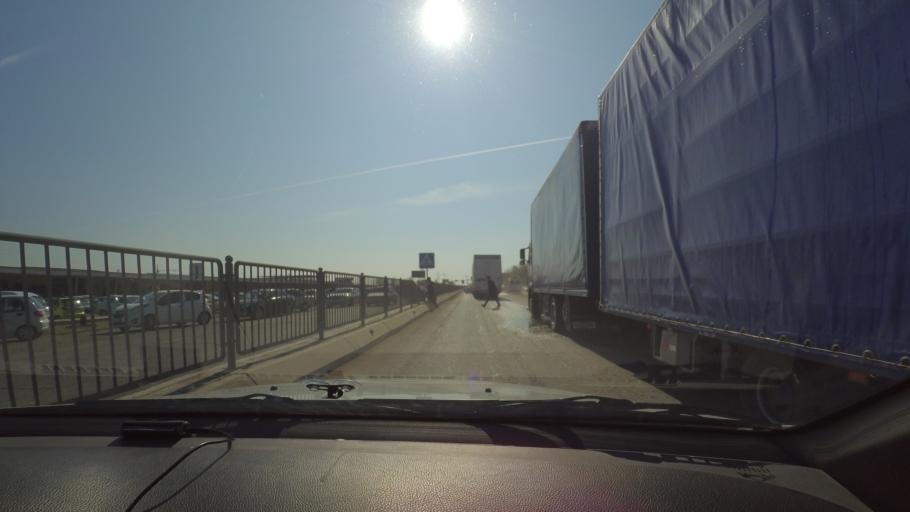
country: UZ
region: Bukhara
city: Bukhara
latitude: 39.8056
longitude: 64.4237
